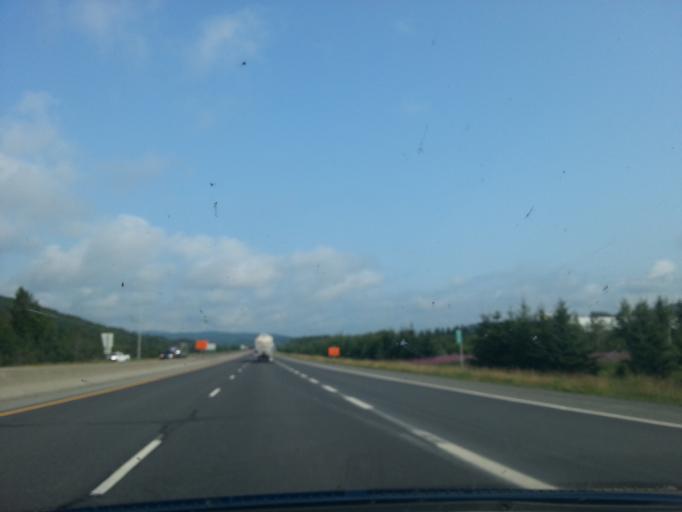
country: CA
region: New Brunswick
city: Edmundston
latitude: 47.3754
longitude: -68.3148
